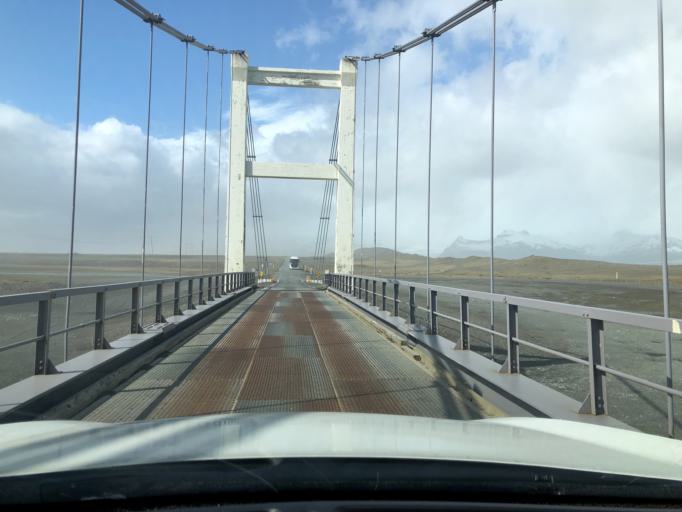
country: IS
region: East
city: Hoefn
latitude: 64.0455
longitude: -16.1805
